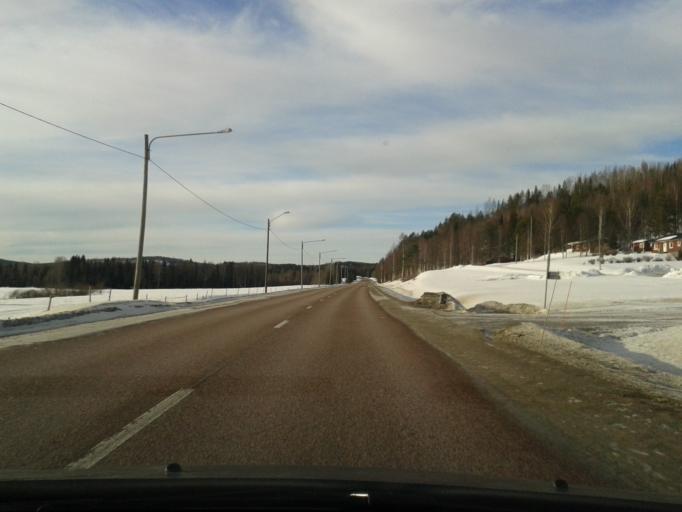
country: SE
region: Vaesternorrland
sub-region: OErnskoeldsviks Kommun
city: Bredbyn
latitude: 63.3909
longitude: 18.3444
